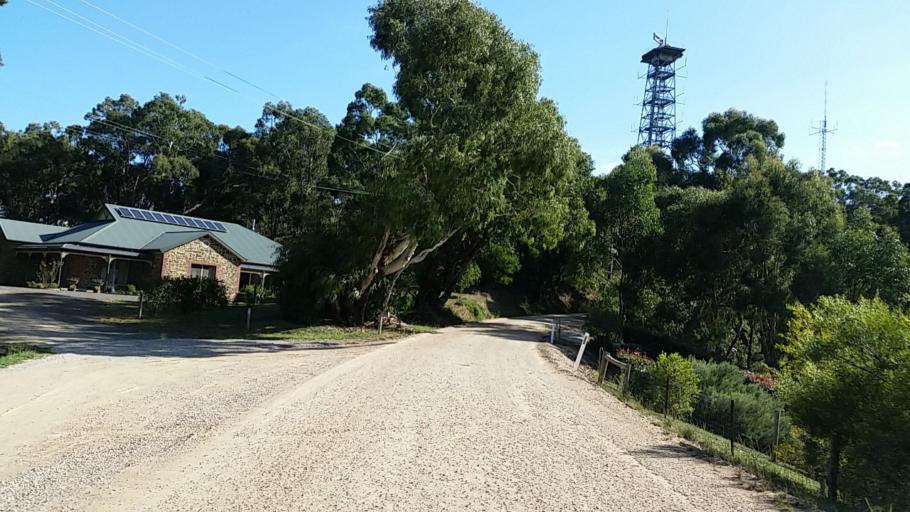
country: AU
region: South Australia
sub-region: Adelaide Hills
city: Adelaide Hills
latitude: -34.9536
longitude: 138.7175
